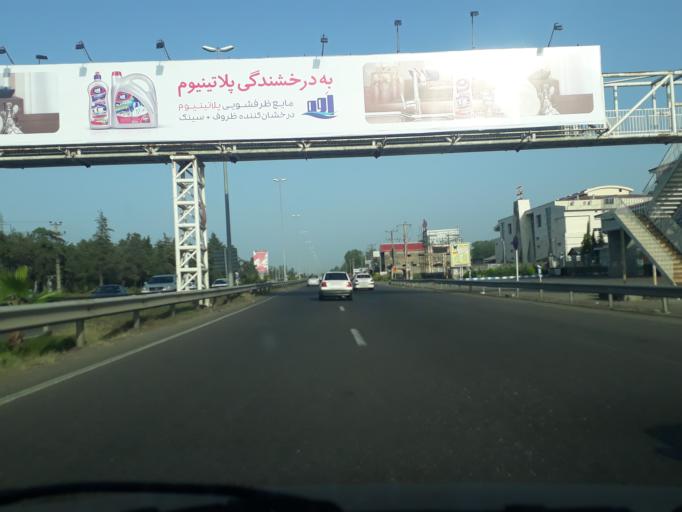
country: IR
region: Gilan
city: Bandar-e Anzali
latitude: 37.4613
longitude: 49.5679
